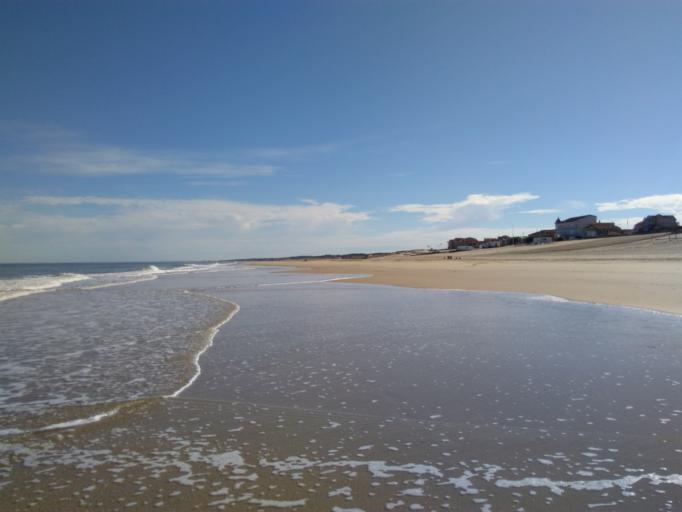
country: FR
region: Aquitaine
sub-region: Departement de la Gironde
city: Soulac-sur-Mer
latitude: 45.5144
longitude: -1.1316
